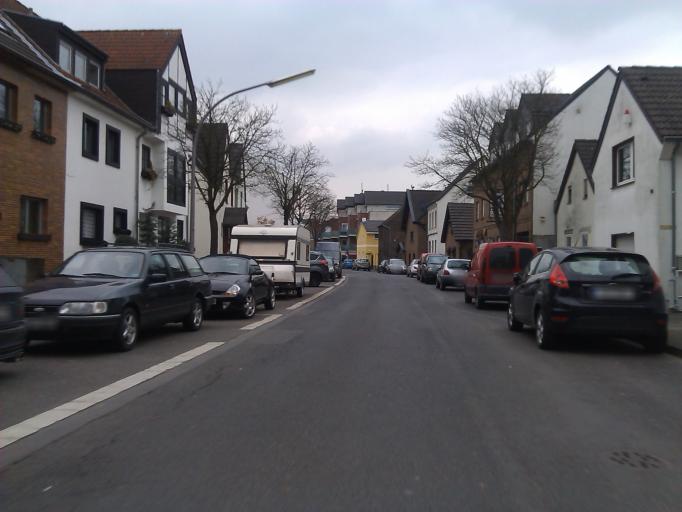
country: DE
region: North Rhine-Westphalia
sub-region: Regierungsbezirk Koln
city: Leverkusen
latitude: 51.0238
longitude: 6.9603
